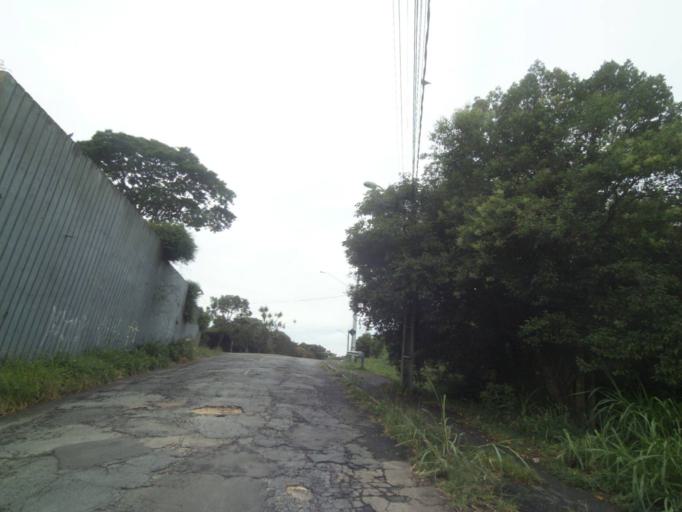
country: BR
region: Parana
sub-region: Curitiba
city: Curitiba
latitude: -25.4121
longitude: -49.2852
